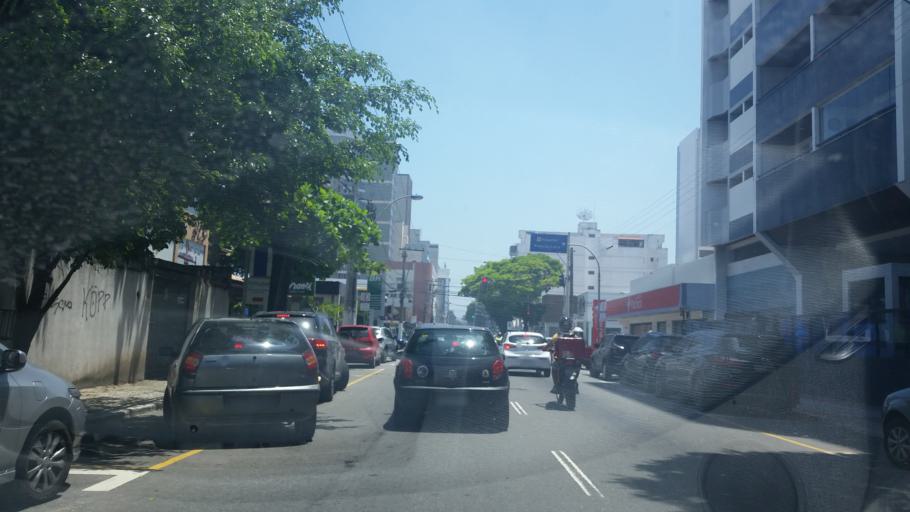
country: BR
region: Espirito Santo
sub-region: Vila Velha
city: Vila Velha
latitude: -20.3358
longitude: -40.2866
